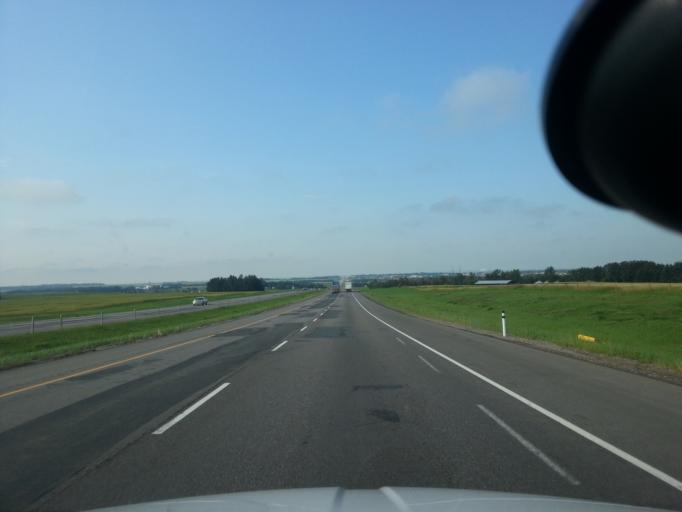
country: CA
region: Alberta
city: Penhold
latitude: 52.0540
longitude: -113.8963
